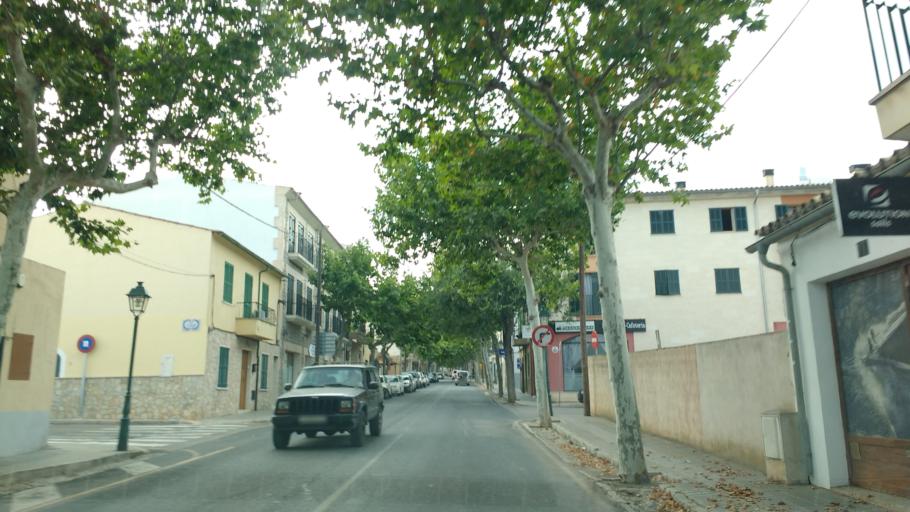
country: ES
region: Balearic Islands
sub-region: Illes Balears
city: Alaro
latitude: 39.7028
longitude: 2.7939
